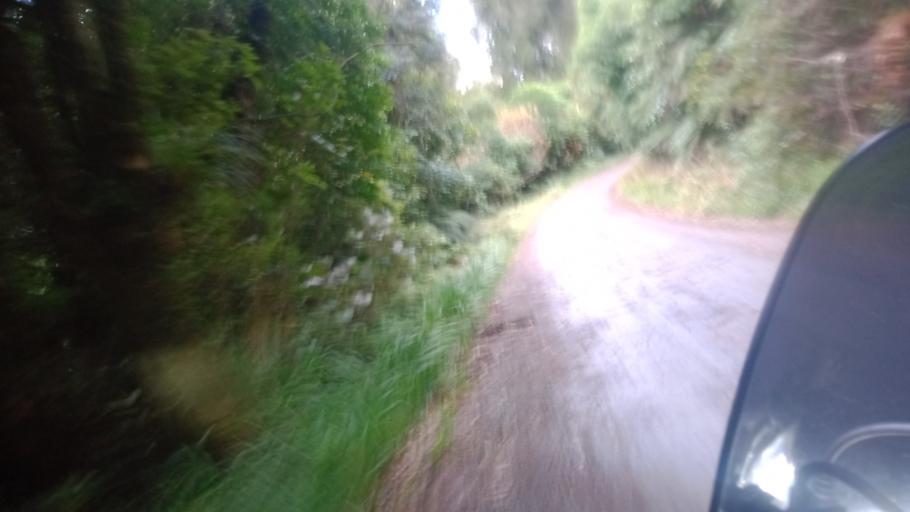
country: NZ
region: Hawke's Bay
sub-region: Wairoa District
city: Wairoa
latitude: -38.7304
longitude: 177.0890
